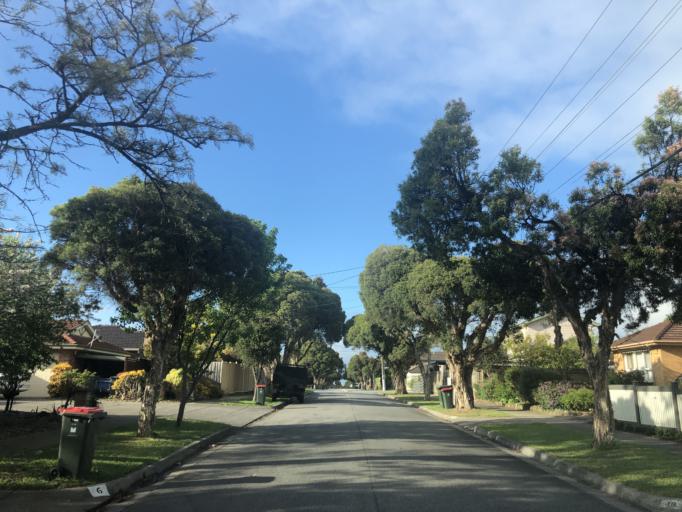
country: AU
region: Victoria
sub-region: Monash
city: Ashwood
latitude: -37.8850
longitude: 145.1197
